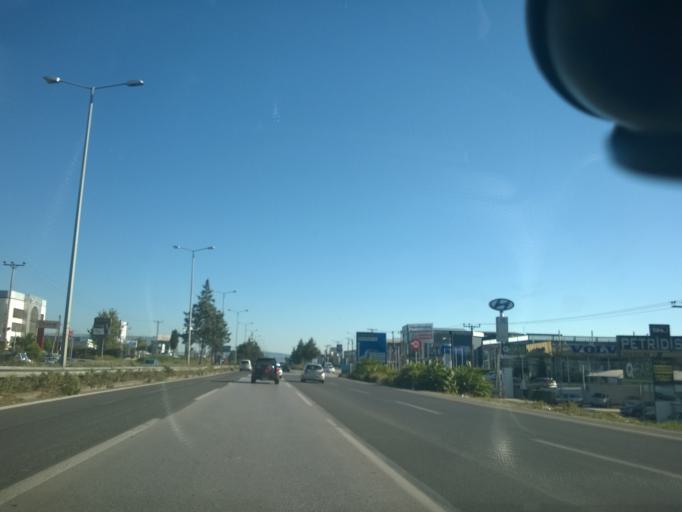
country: GR
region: Central Macedonia
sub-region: Nomos Thessalonikis
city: Pylaia
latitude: 40.5757
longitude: 22.9818
